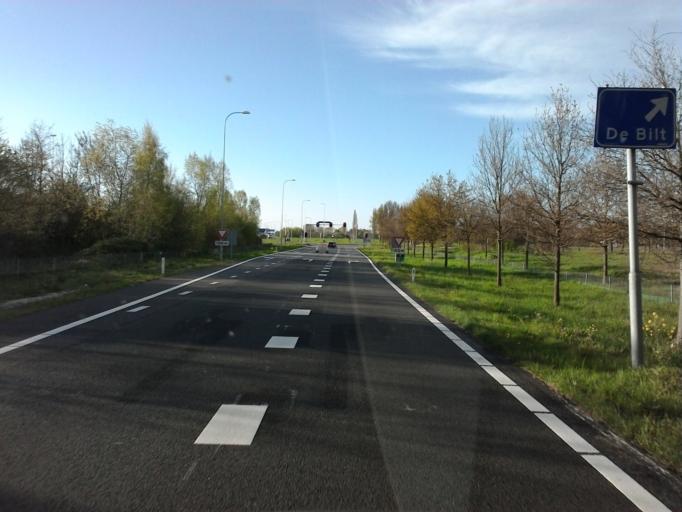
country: NL
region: Utrecht
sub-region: Gemeente De Bilt
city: De Bilt
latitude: 52.1023
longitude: 5.1549
